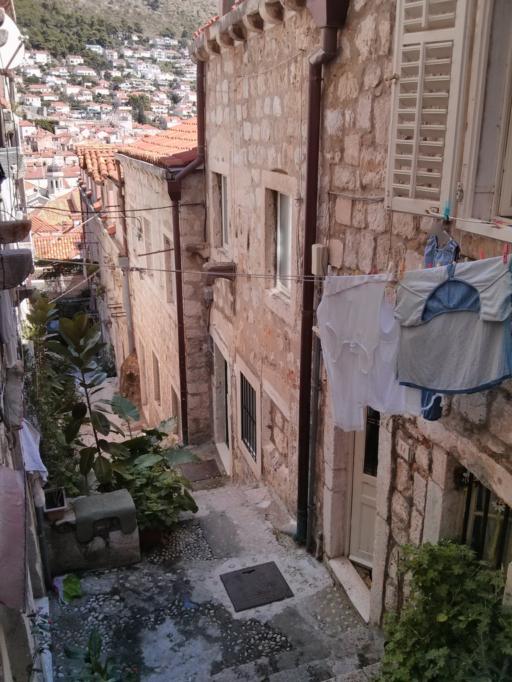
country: HR
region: Dubrovacko-Neretvanska
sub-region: Grad Dubrovnik
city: Dubrovnik
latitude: 42.6397
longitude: 18.1076
